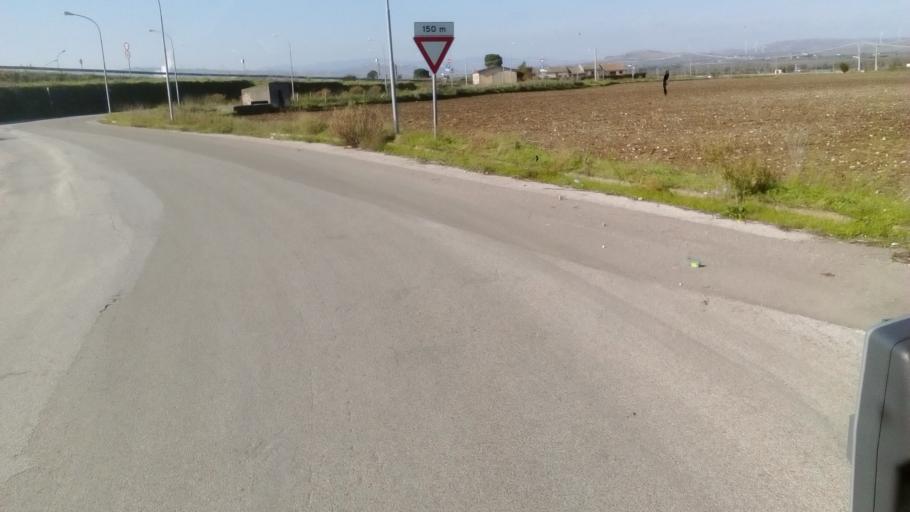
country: IT
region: Basilicate
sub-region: Provincia di Potenza
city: Melfi
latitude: 41.0774
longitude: 15.6742
